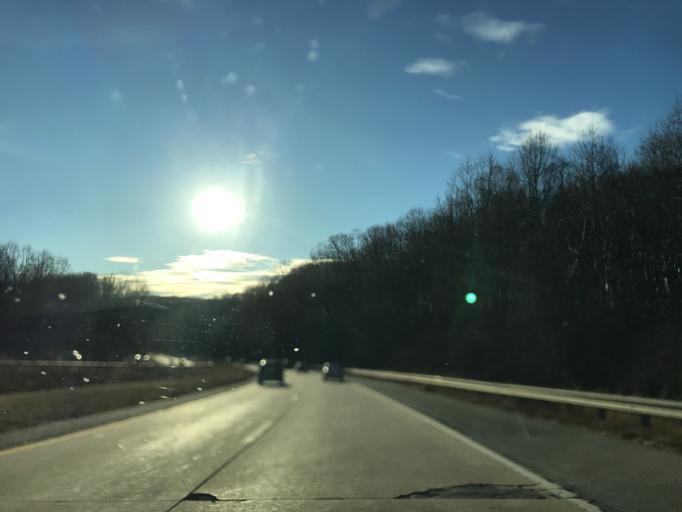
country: US
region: Maryland
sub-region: Howard County
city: Fulton
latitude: 39.1359
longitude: -76.9145
